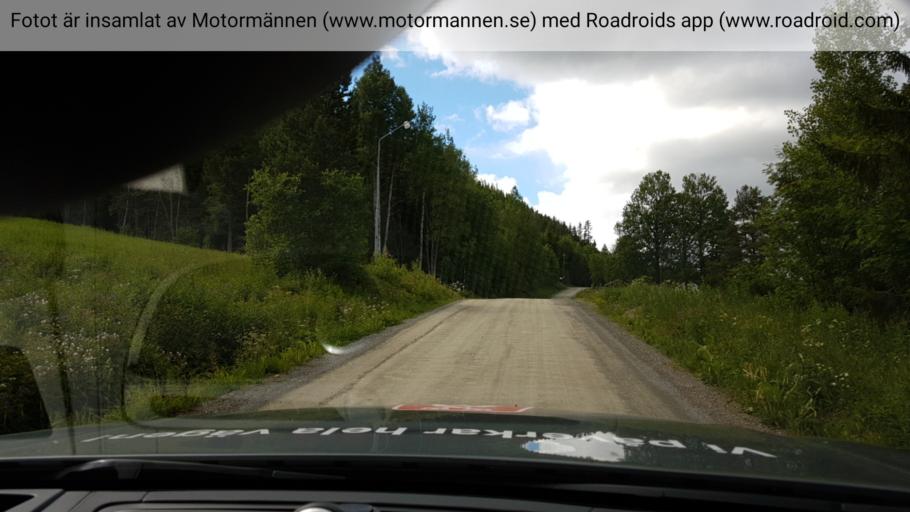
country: SE
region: Jaemtland
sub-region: Bergs Kommun
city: Hoverberg
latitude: 62.9240
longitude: 14.3024
